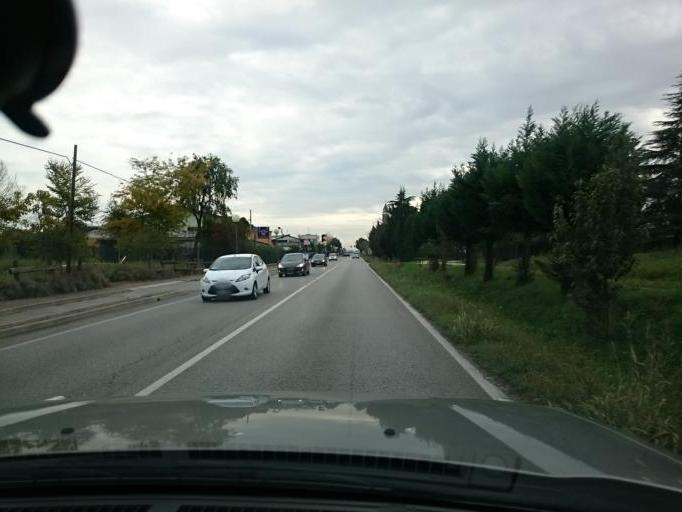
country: IT
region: Veneto
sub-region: Provincia di Padova
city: Sant'Angelo di Piove di Sacco
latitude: 45.3237
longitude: 11.9959
